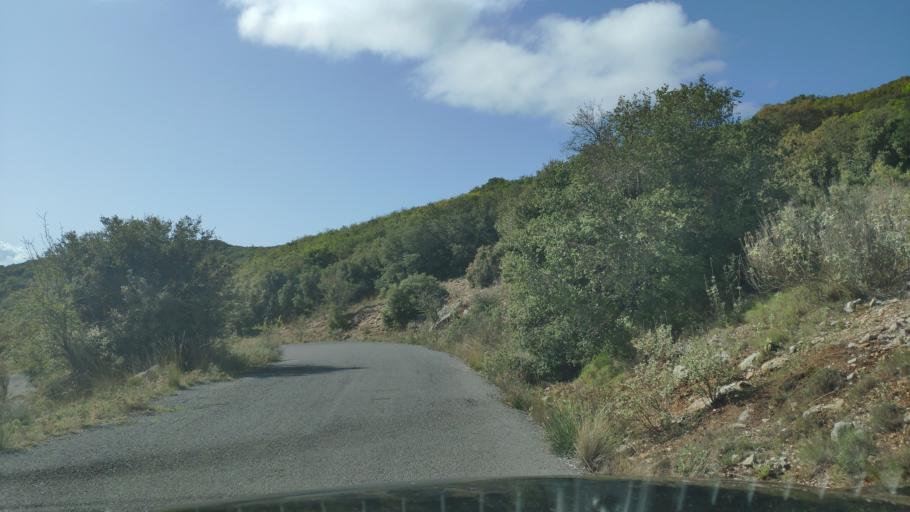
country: GR
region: Peloponnese
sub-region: Nomos Arkadias
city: Dimitsana
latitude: 37.5741
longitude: 22.0012
